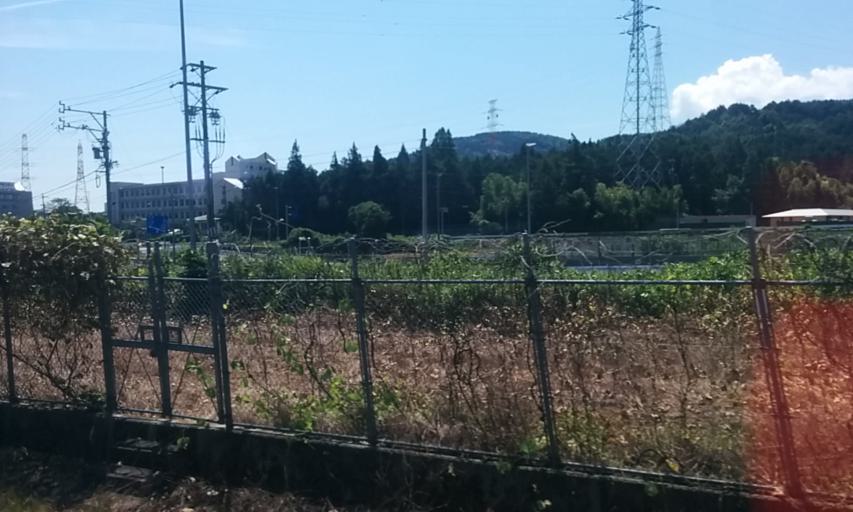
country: JP
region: Gifu
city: Tarui
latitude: 35.3717
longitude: 136.5052
